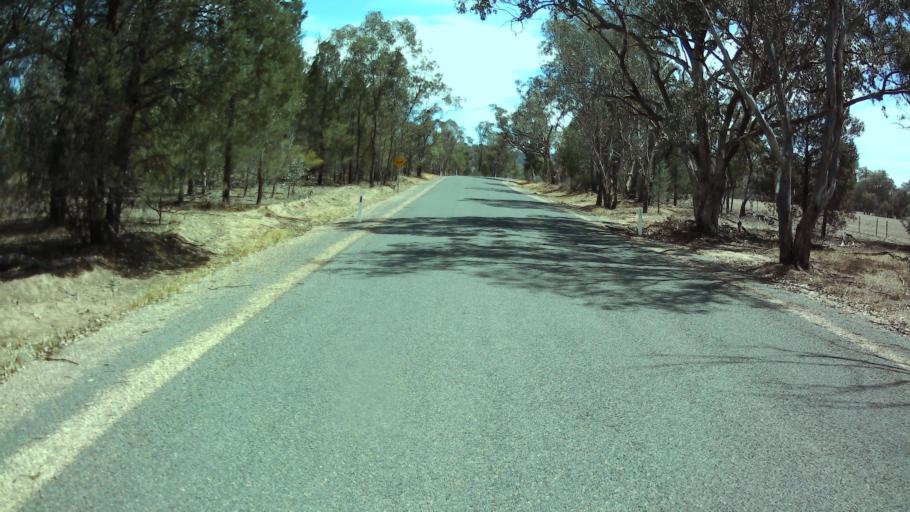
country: AU
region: New South Wales
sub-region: Weddin
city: Grenfell
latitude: -33.7692
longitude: 148.2049
